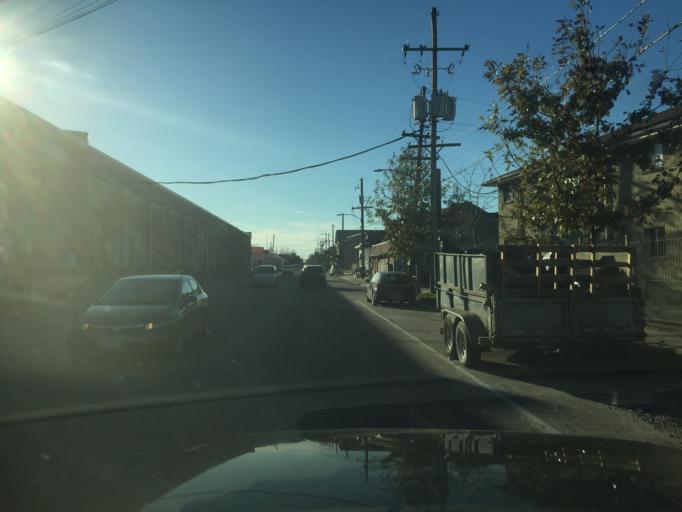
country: US
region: Louisiana
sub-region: Jefferson Parish
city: Marrero
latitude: 29.9179
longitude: -90.0927
